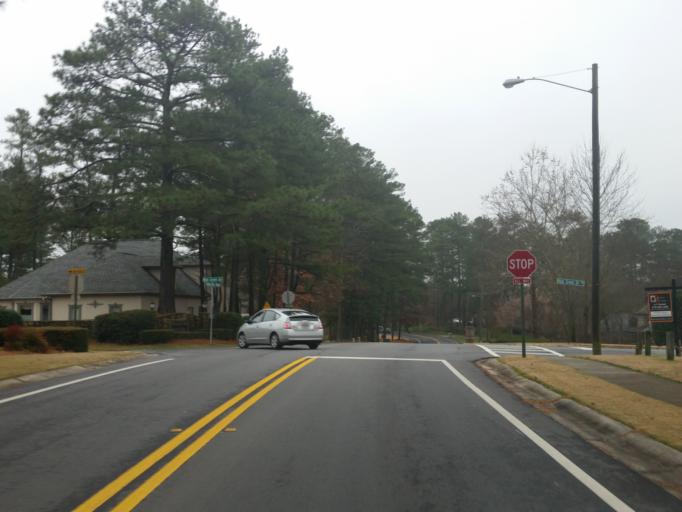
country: US
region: Georgia
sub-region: Fulton County
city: Sandy Springs
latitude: 33.9706
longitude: -84.4393
